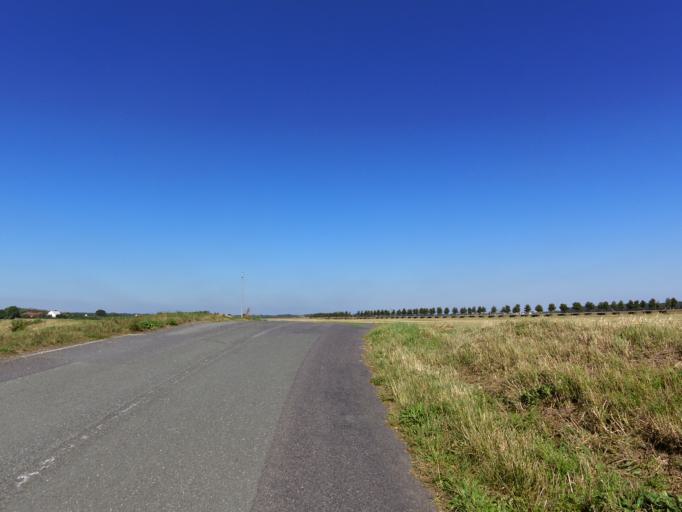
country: DE
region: Saxony
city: Riesa
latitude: 51.3483
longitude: 13.2794
